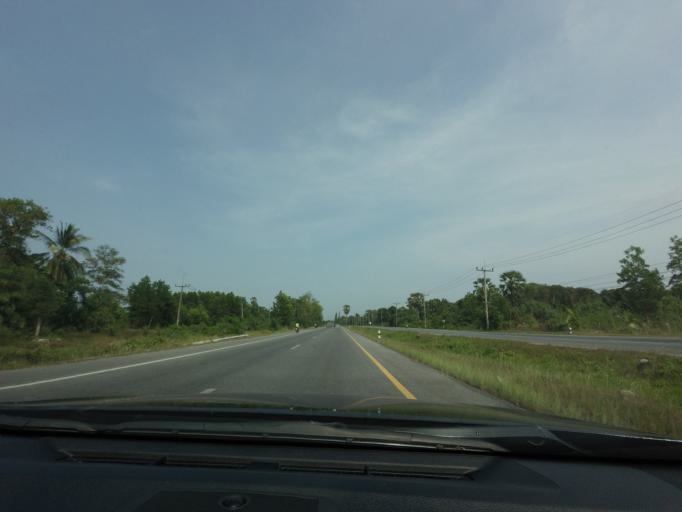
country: TH
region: Pattani
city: Yaring
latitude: 6.8251
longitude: 101.3961
